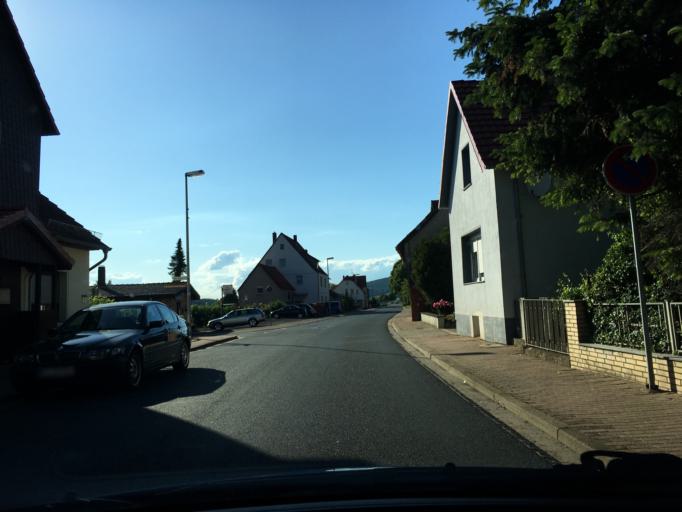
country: DE
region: Lower Saxony
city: Duingen
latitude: 52.0080
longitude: 9.6950
